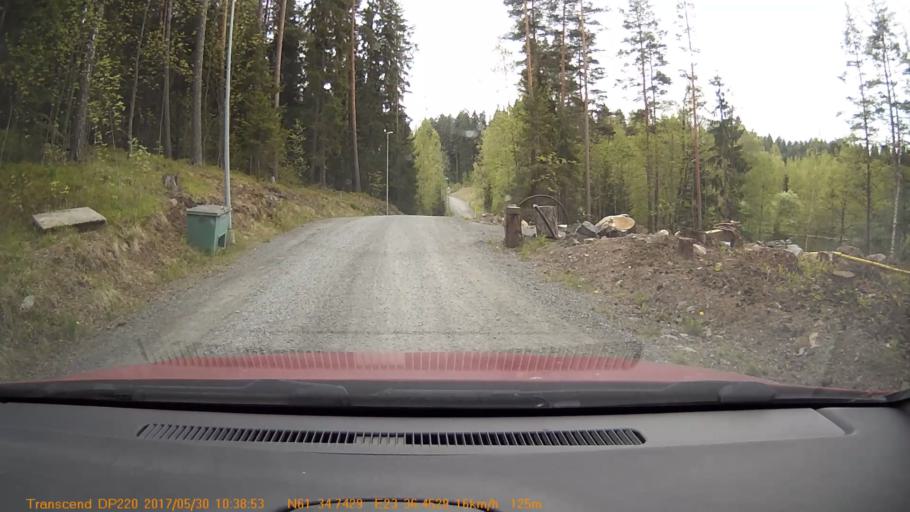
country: FI
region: Pirkanmaa
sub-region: Tampere
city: Yloejaervi
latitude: 61.5789
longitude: 23.6077
